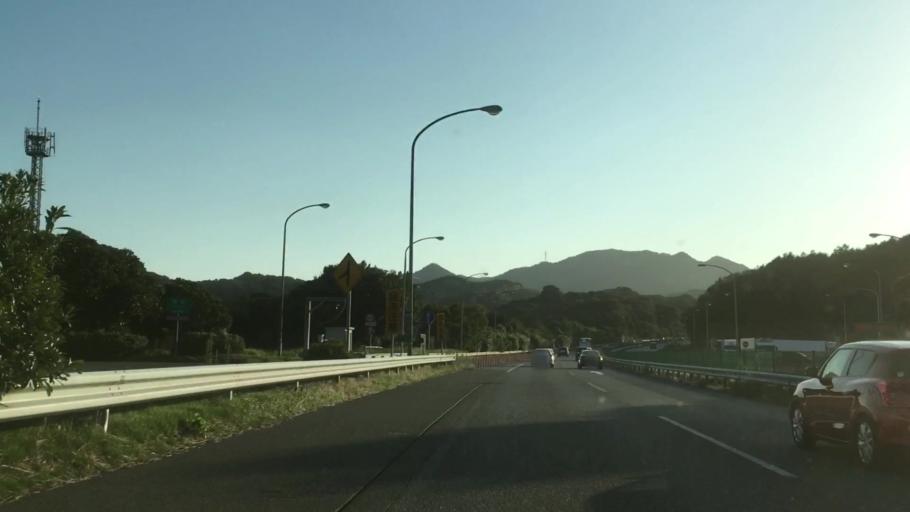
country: JP
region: Yamaguchi
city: Shimonoseki
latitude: 34.0505
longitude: 131.0045
